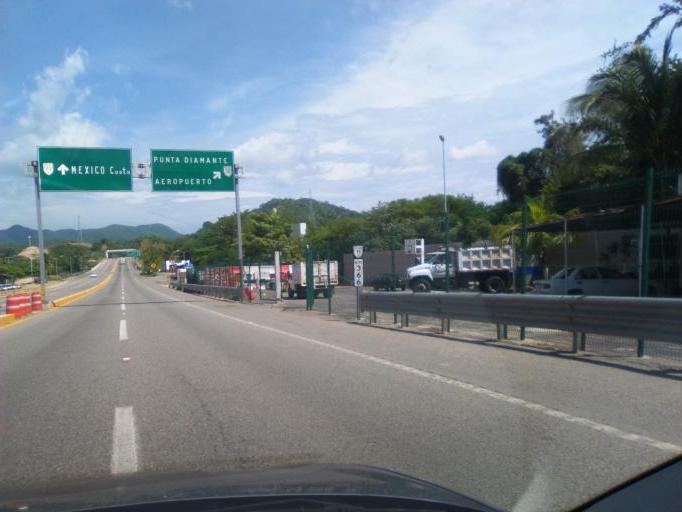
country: MX
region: Guerrero
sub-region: Acapulco de Juarez
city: Colonia Nueva Revolucion
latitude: 16.9233
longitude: -99.8111
